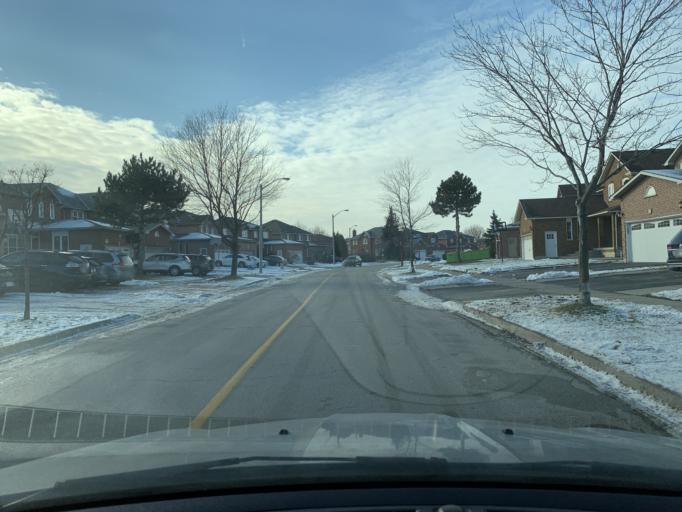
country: CA
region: Ontario
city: Etobicoke
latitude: 43.7209
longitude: -79.6171
